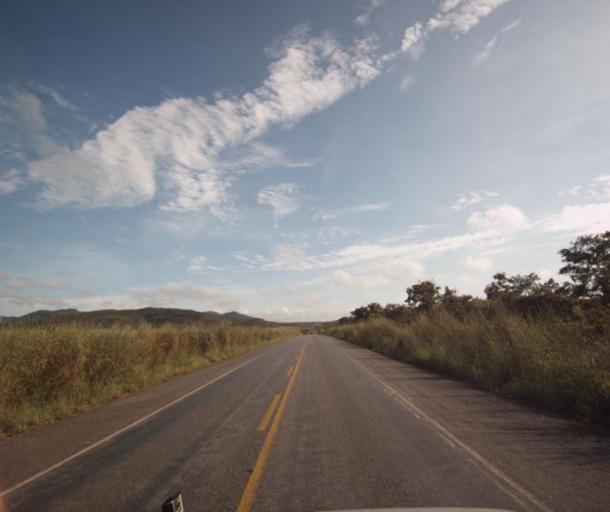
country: BR
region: Goias
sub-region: Pirenopolis
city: Pirenopolis
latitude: -15.5625
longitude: -48.6222
